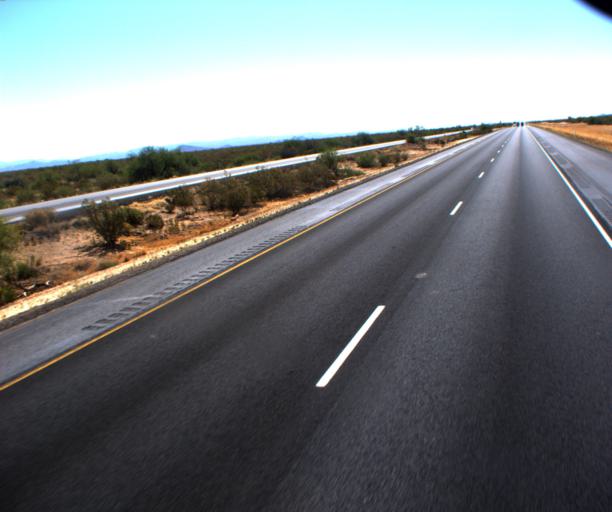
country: US
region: Arizona
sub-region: Yavapai County
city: Congress
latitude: 34.0836
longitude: -112.8940
